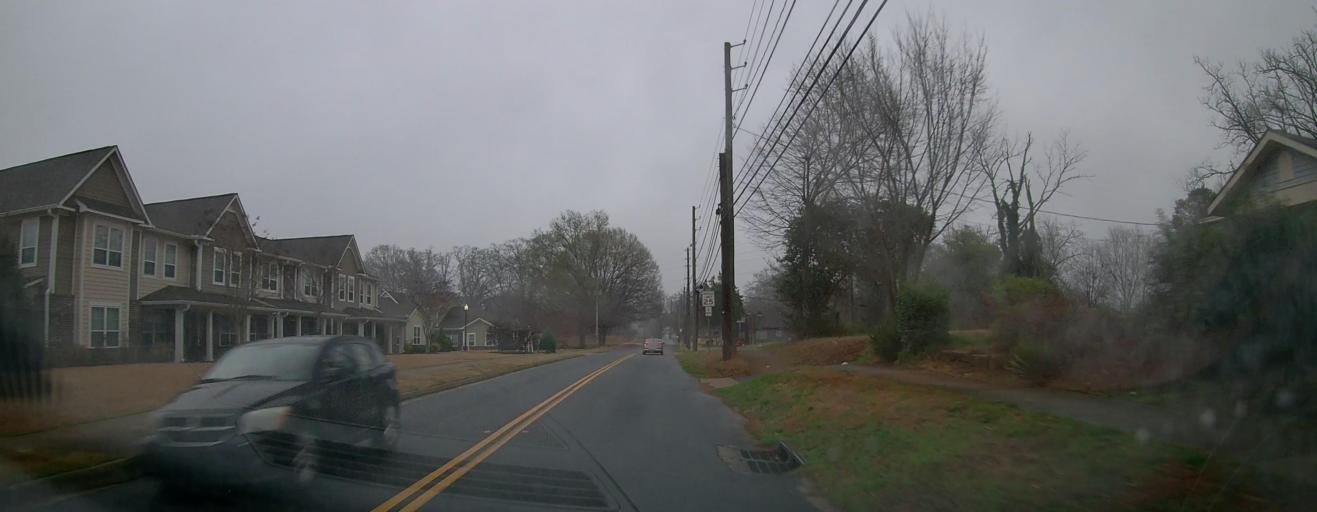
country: US
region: Georgia
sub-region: Spalding County
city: Griffin
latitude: 33.2425
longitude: -84.2756
